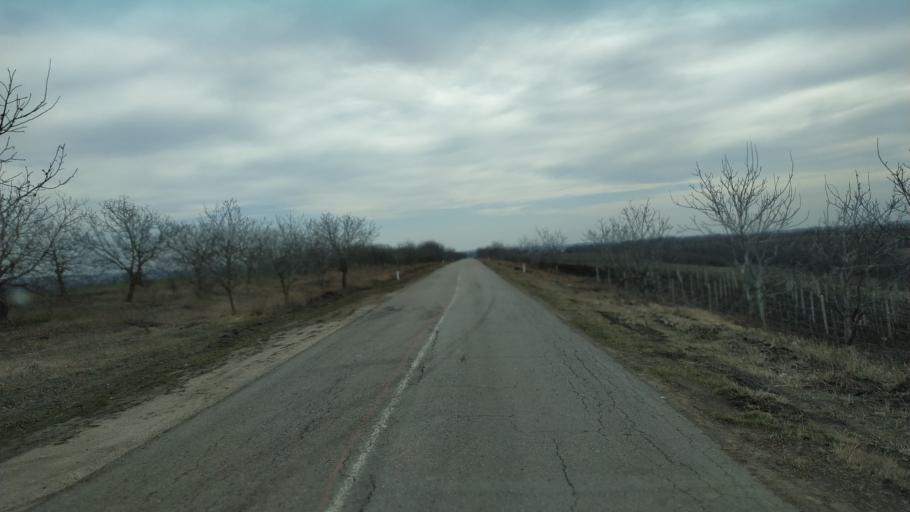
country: MD
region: Nisporeni
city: Nisporeni
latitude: 46.9510
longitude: 28.2388
